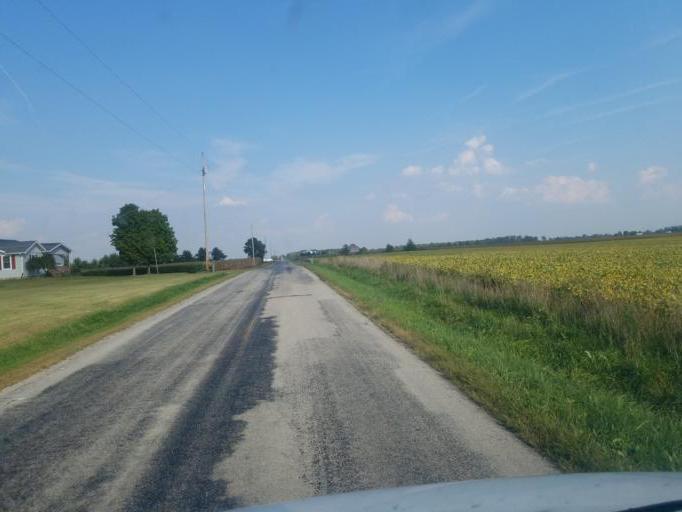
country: US
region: Ohio
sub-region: Wyandot County
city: Carey
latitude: 40.9050
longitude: -83.4556
